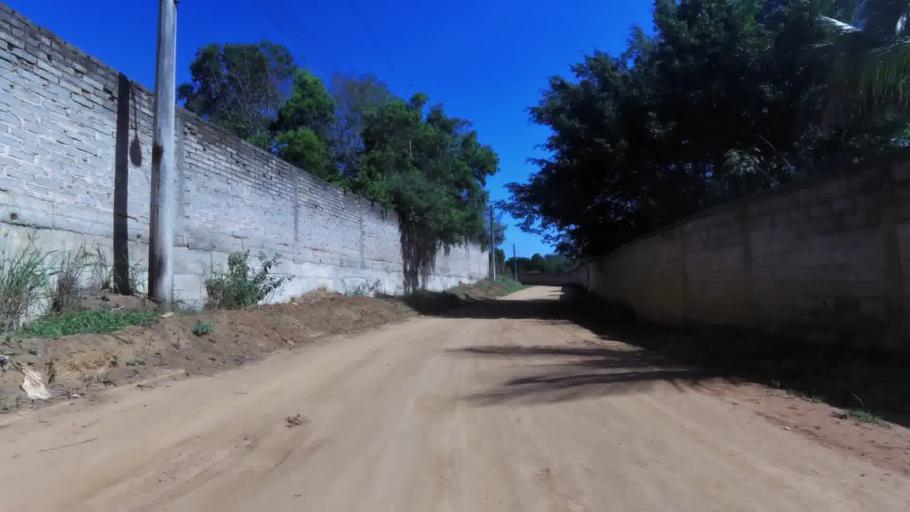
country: BR
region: Espirito Santo
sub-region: Guarapari
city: Guarapari
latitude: -20.7349
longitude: -40.5565
